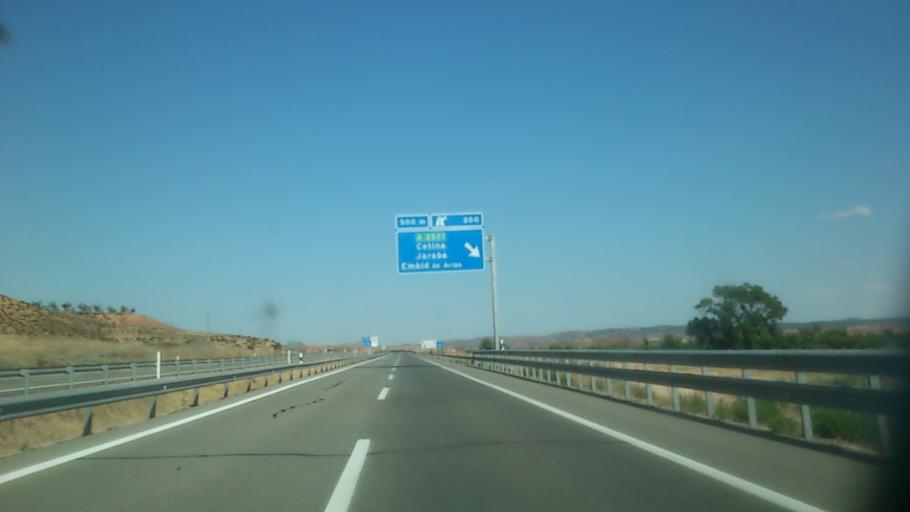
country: ES
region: Aragon
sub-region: Provincia de Zaragoza
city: Cetina
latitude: 41.3056
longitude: -1.9794
